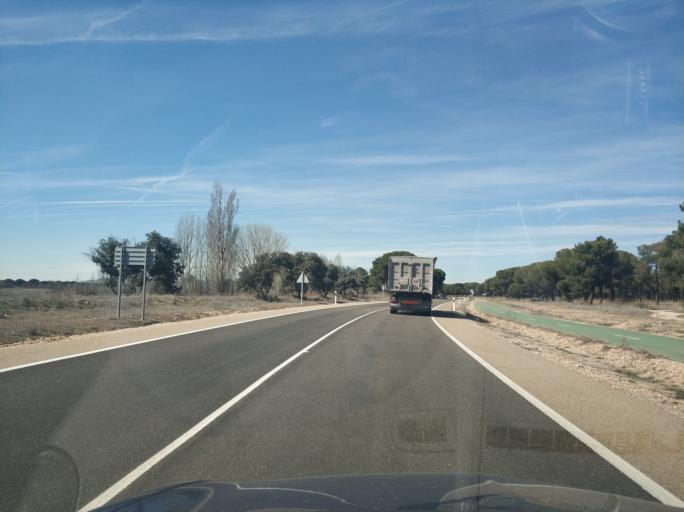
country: ES
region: Castille and Leon
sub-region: Provincia de Valladolid
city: Arroyo
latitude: 41.5624
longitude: -4.7893
